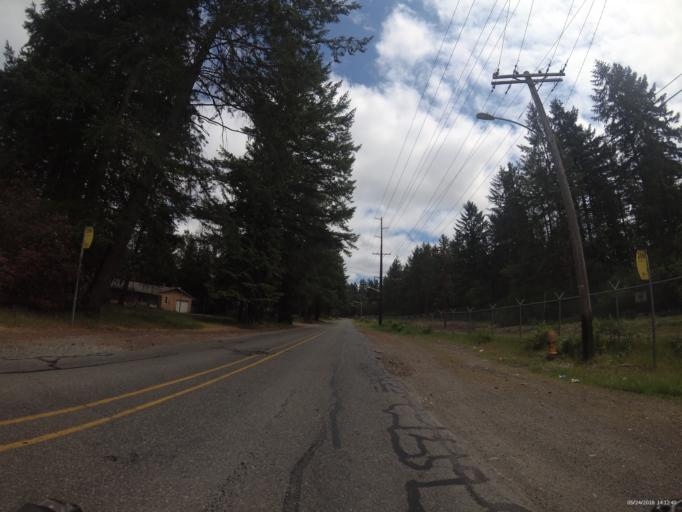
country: US
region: Washington
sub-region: Pierce County
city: McChord Air Force Base
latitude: 47.1402
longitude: -122.5127
